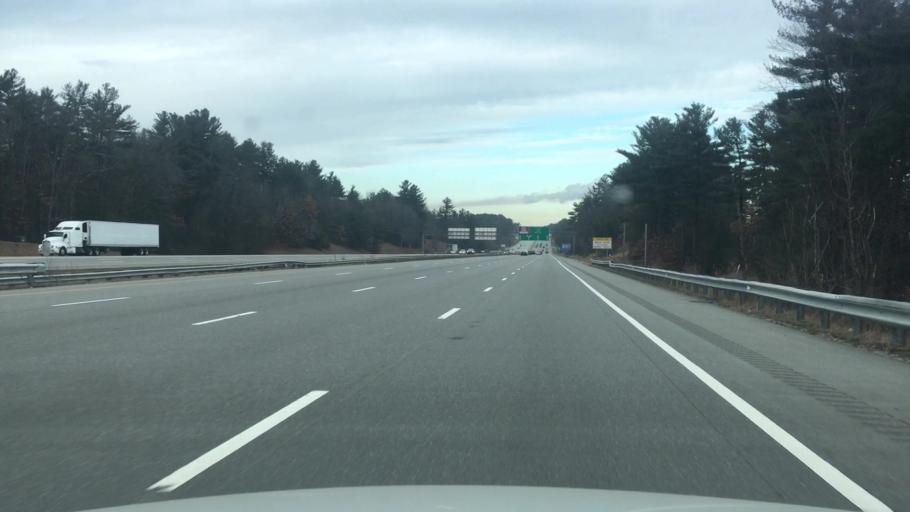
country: US
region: New Hampshire
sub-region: Merrimack County
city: Hooksett
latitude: 43.0615
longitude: -71.4710
